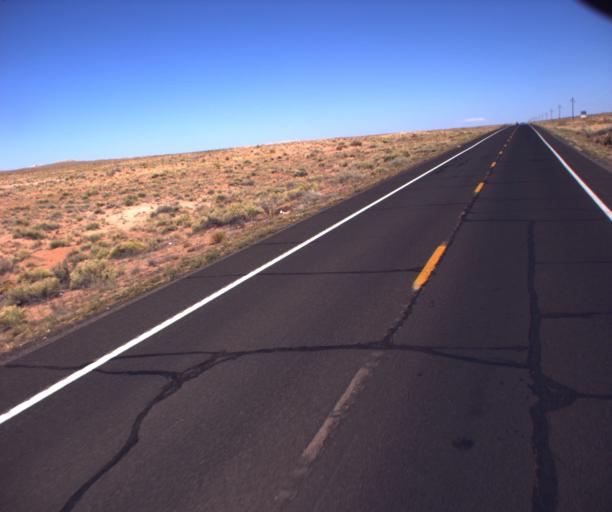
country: US
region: Arizona
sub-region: Coconino County
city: Tuba City
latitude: 36.1322
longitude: -111.1844
